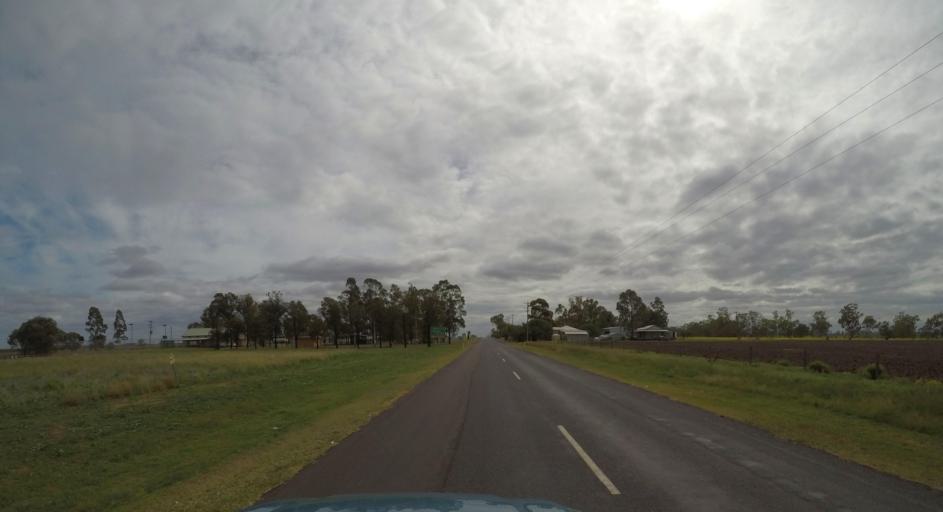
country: AU
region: Queensland
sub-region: Western Downs
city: Dalby
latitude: -26.9648
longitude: 151.2177
